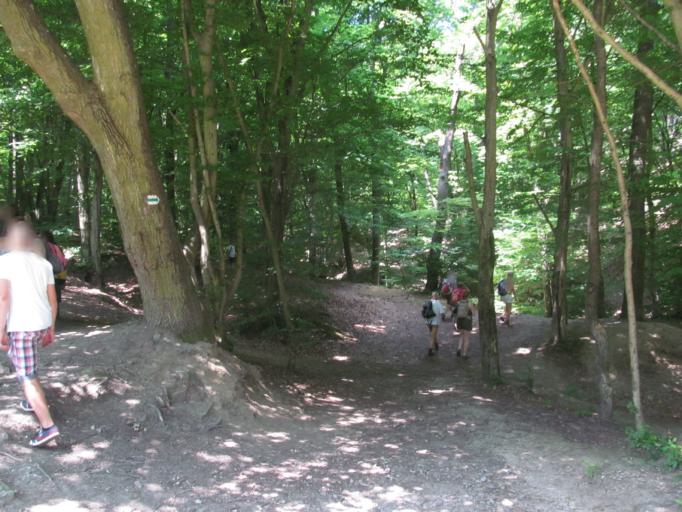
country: HU
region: Komarom-Esztergom
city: Pilismarot
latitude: 47.7441
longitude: 18.9010
